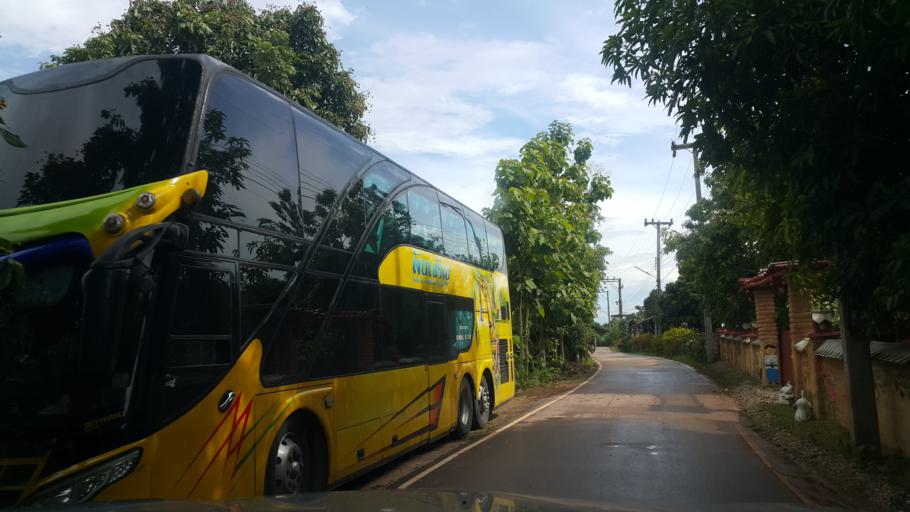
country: TH
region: Chiang Mai
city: Mae Taeng
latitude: 19.2147
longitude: 99.0086
